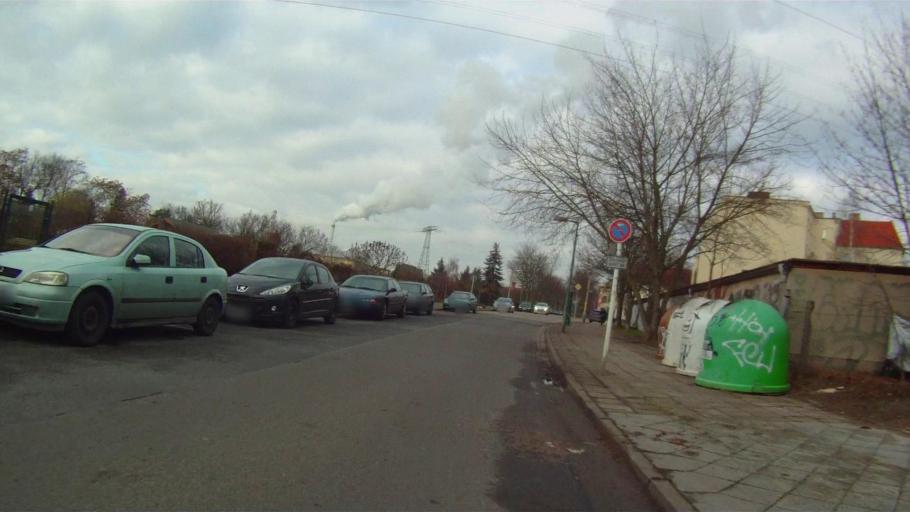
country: DE
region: Berlin
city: Karlshorst
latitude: 52.4882
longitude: 13.5158
